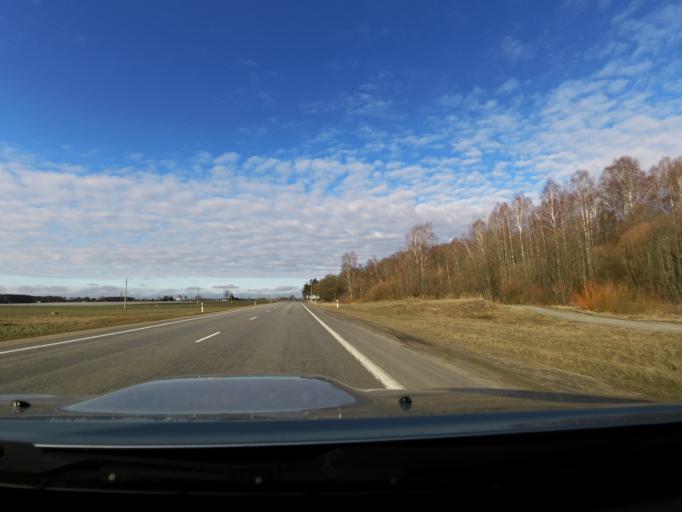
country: LT
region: Panevezys
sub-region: Panevezys City
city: Panevezys
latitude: 55.7343
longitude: 24.2492
